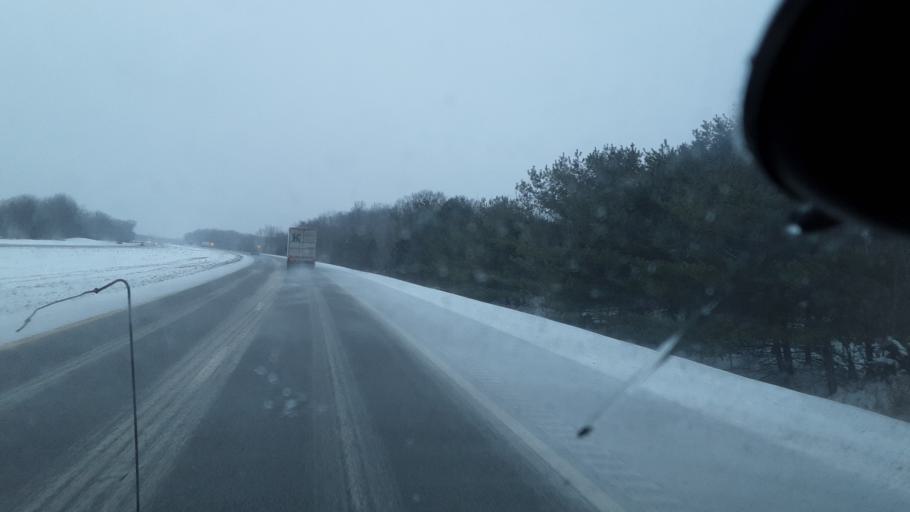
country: US
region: Ohio
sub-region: Franklin County
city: Reynoldsburg
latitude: 39.9510
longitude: -82.7495
